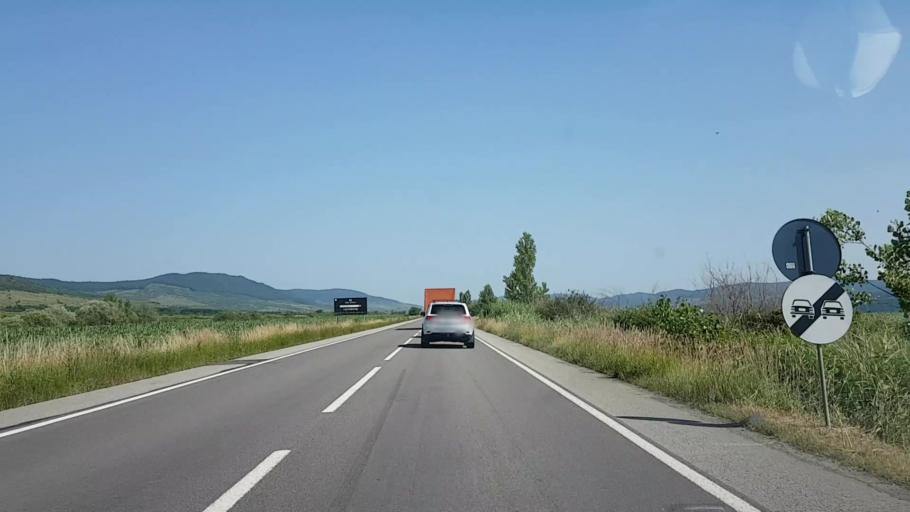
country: RO
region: Bistrita-Nasaud
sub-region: Comuna Sieu-Odorhei
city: Sieu-Odorhei
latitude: 47.1249
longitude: 24.3212
